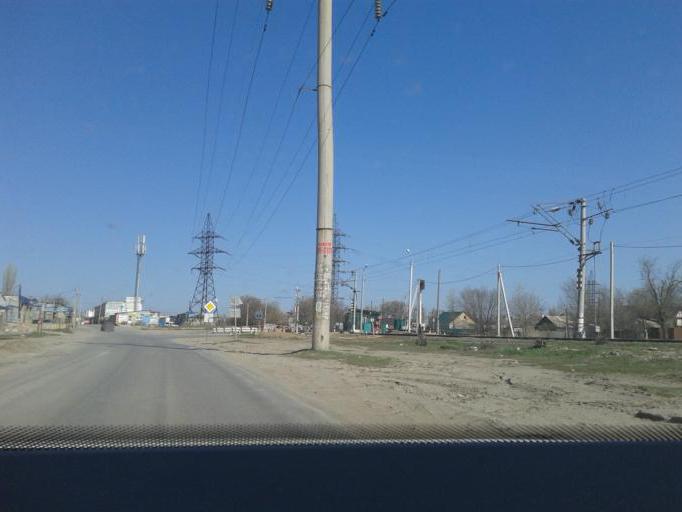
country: RU
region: Volgograd
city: Volgograd
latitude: 48.6783
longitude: 44.4640
